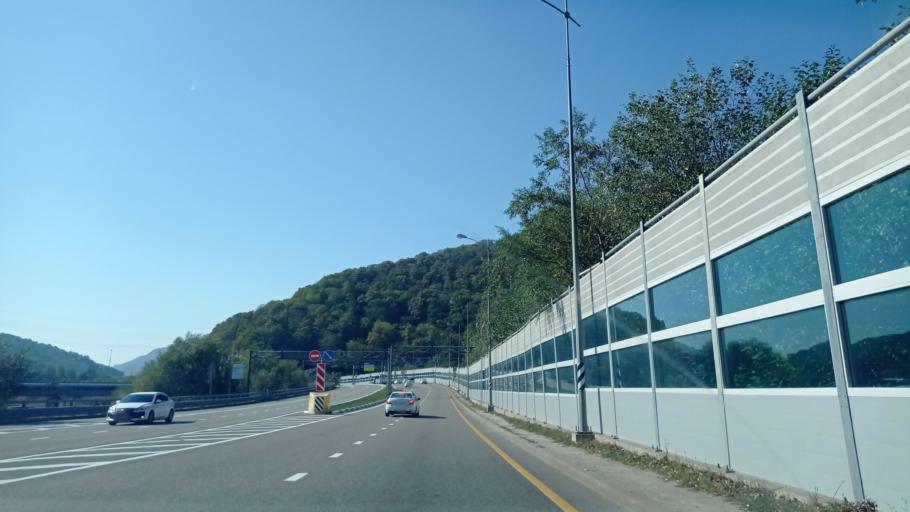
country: RU
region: Krasnodarskiy
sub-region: Sochi City
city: Krasnaya Polyana
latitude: 43.6868
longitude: 40.2485
